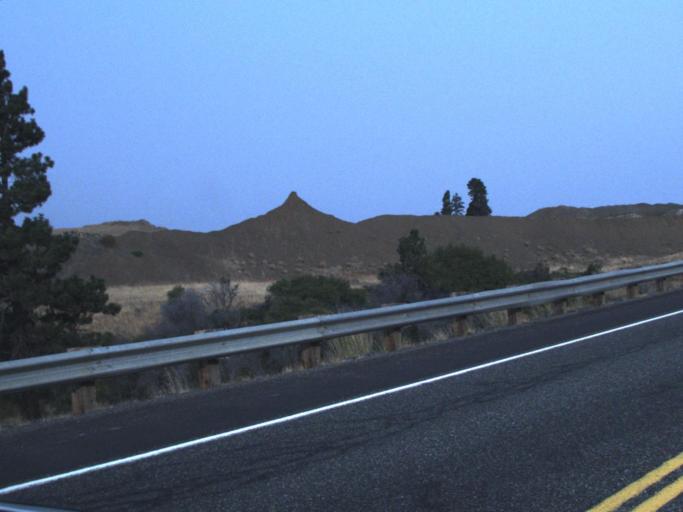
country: US
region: Washington
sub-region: Kittitas County
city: Ellensburg
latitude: 47.1621
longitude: -120.7046
